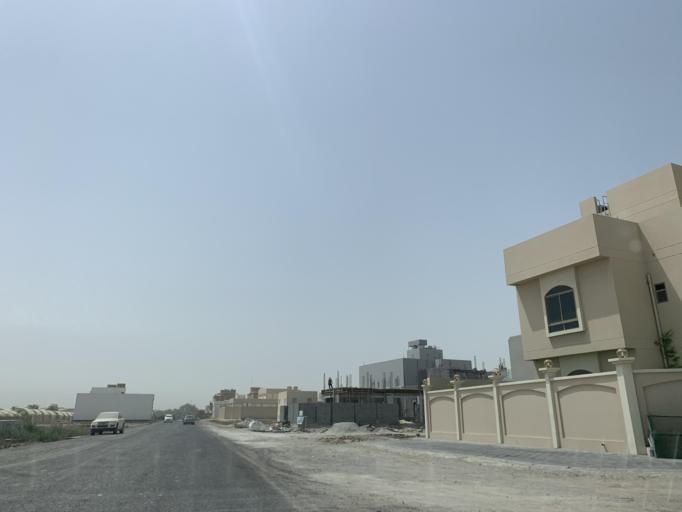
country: BH
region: Northern
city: Madinat `Isa
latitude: 26.1752
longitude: 50.5271
